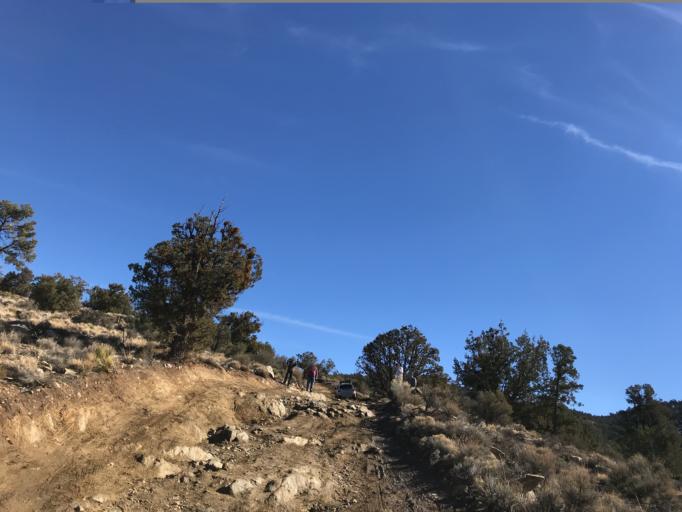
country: US
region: California
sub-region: San Bernardino County
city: Big Bear City
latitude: 34.2516
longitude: -116.7265
